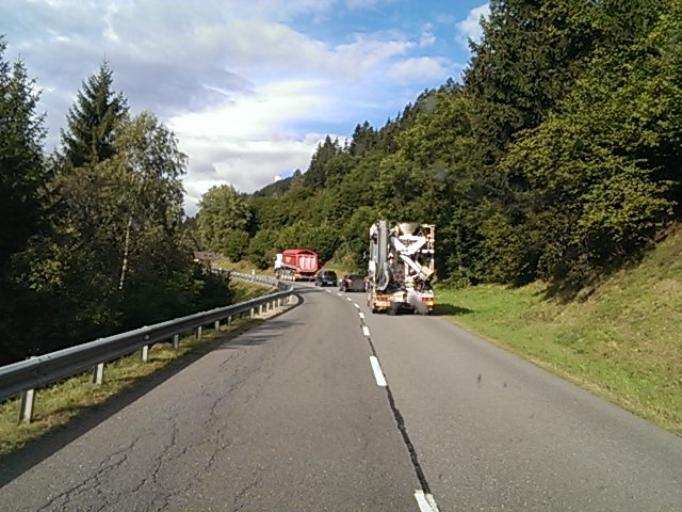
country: IT
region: Trentino-Alto Adige
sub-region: Bolzano
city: Ultimo - Ulten
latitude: 46.5648
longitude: 11.0460
